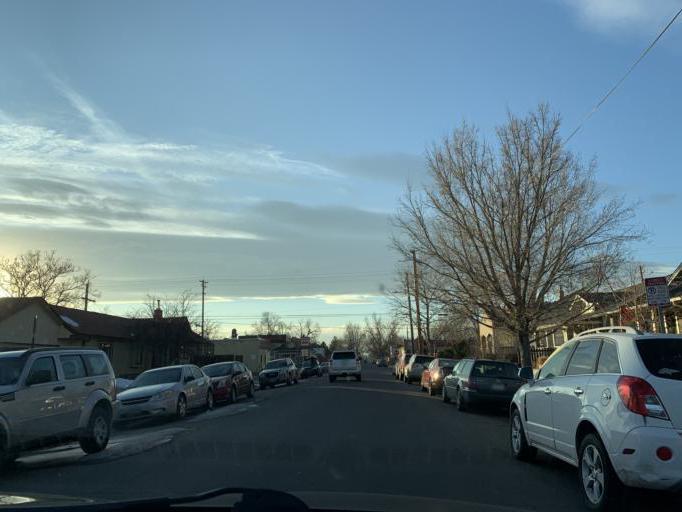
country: US
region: Colorado
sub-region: Adams County
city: Berkley
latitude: 39.7856
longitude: -105.0334
